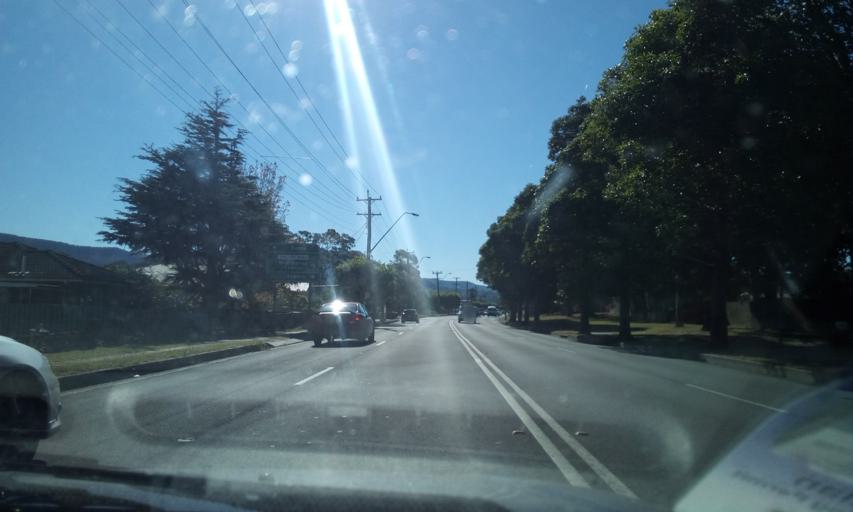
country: AU
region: New South Wales
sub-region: Wollongong
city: Dapto
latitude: -34.5005
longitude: 150.7900
